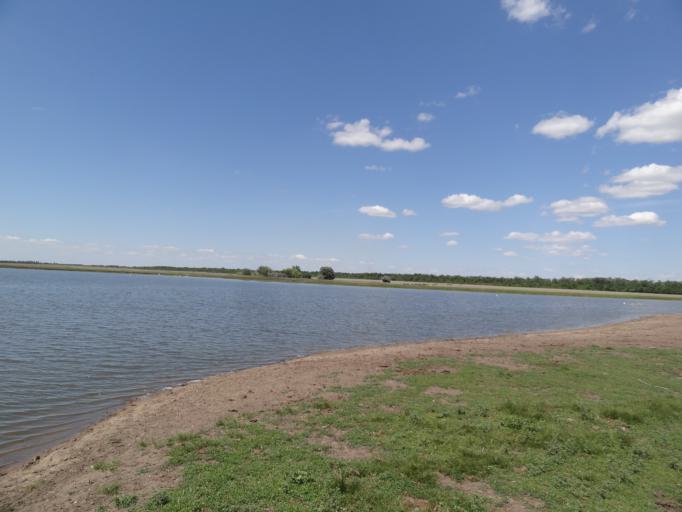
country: RU
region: Saratov
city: Sovetskoye
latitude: 51.2886
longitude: 46.6549
